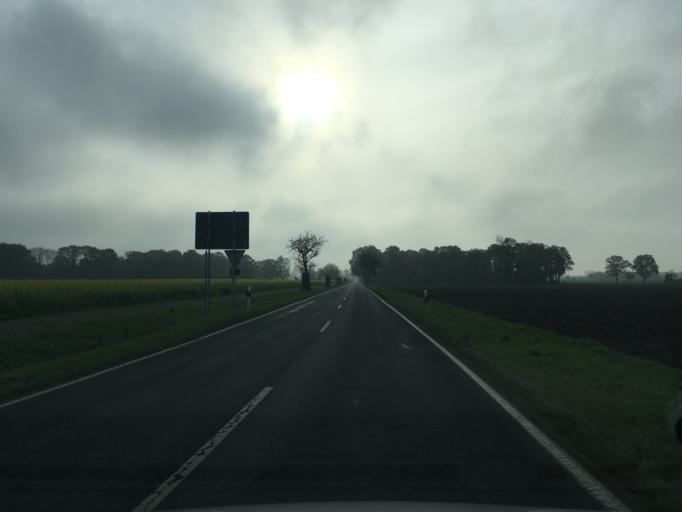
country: DE
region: North Rhine-Westphalia
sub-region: Regierungsbezirk Munster
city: Sudlohn
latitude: 51.9255
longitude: 6.9146
